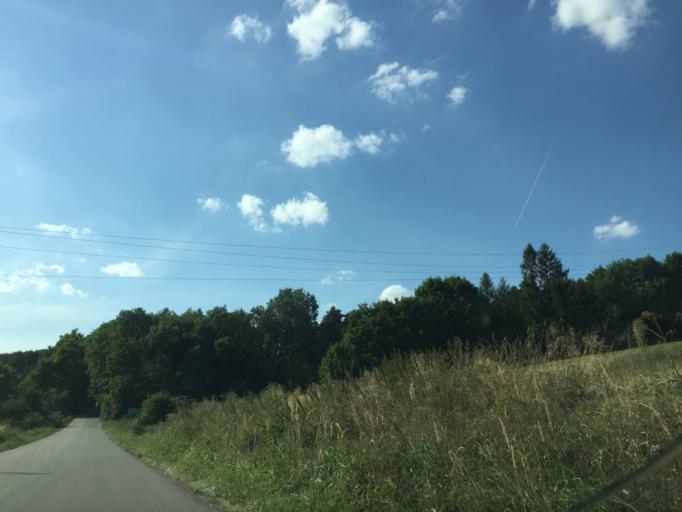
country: PL
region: Swietokrzyskie
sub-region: Powiat jedrzejowski
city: Wodzislaw
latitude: 50.4249
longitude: 20.1328
